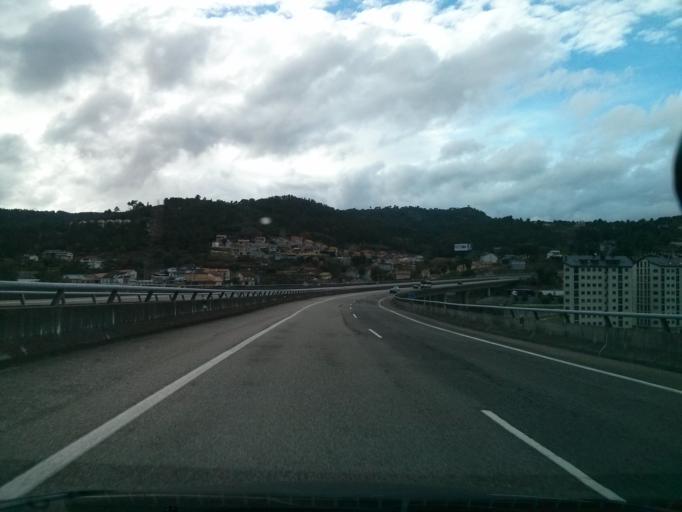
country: ES
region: Galicia
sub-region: Provincia de Ourense
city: Ourense
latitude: 42.3109
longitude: -7.8812
